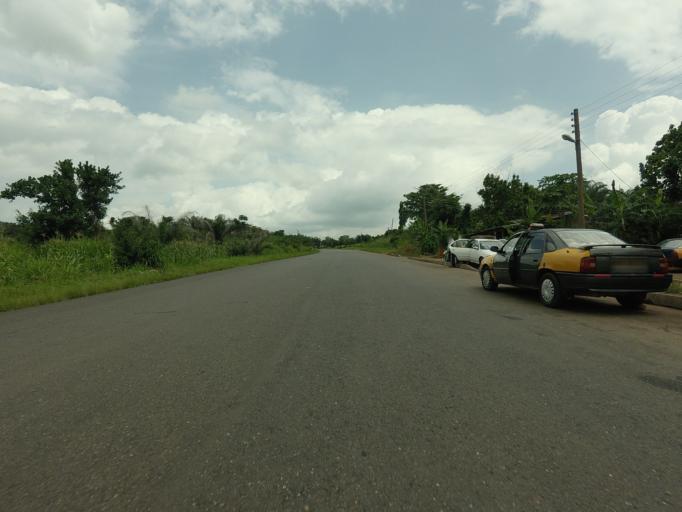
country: GH
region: Volta
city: Ho
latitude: 6.5232
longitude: 0.2215
